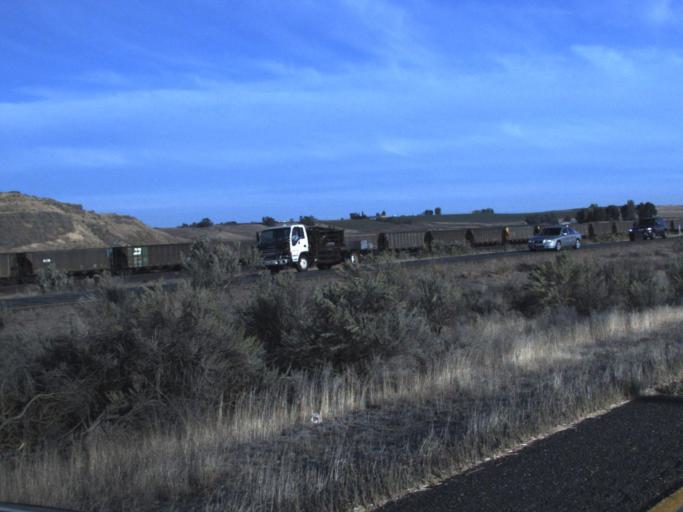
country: US
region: Washington
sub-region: Franklin County
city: Basin City
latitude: 46.4646
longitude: -119.0124
